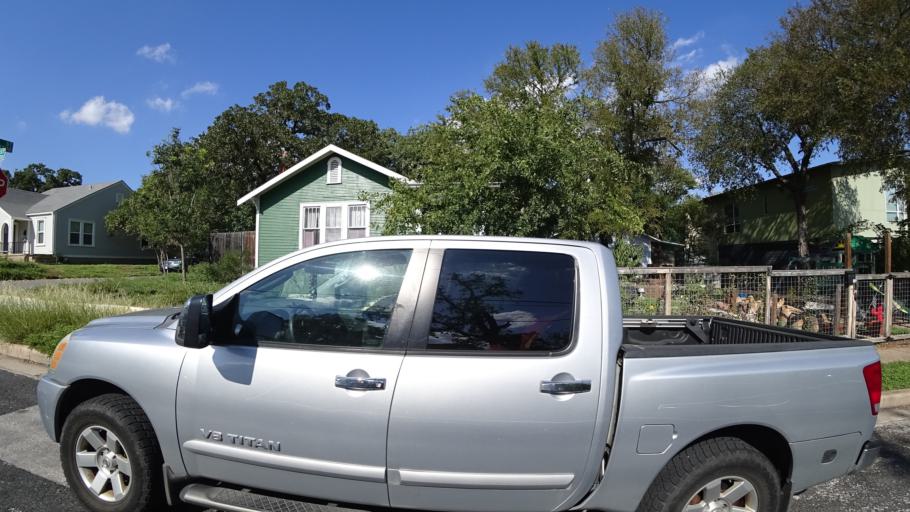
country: US
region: Texas
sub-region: Travis County
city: Austin
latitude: 30.3018
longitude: -97.7406
